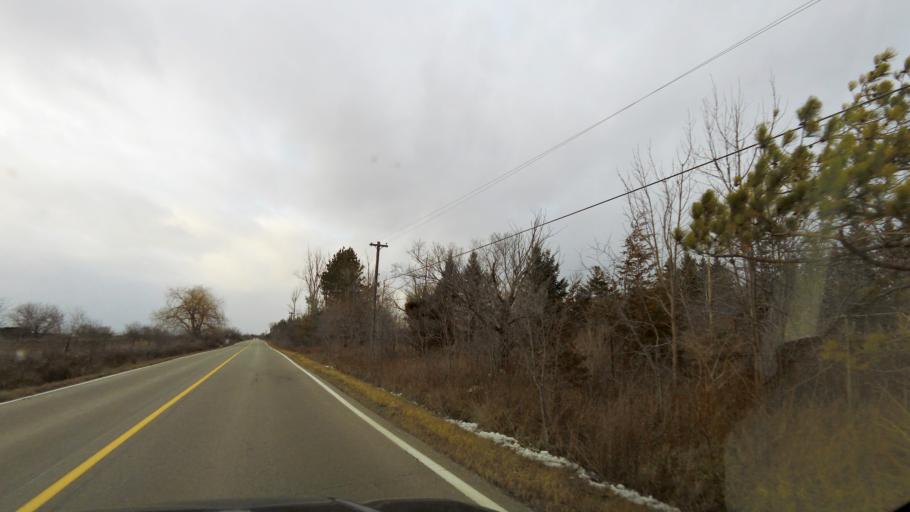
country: CA
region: Ontario
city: Brampton
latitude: 43.8224
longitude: -79.7074
